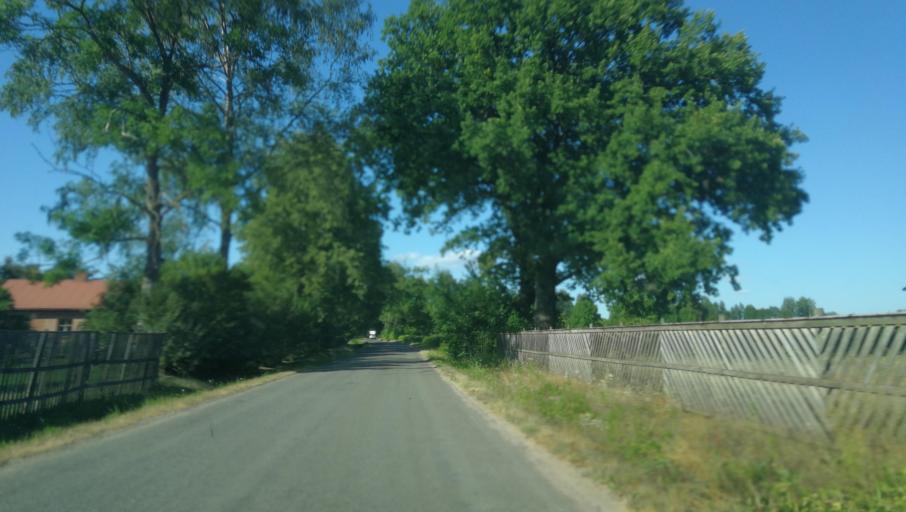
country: LV
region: Cesu Rajons
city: Cesis
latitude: 57.2926
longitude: 25.2329
